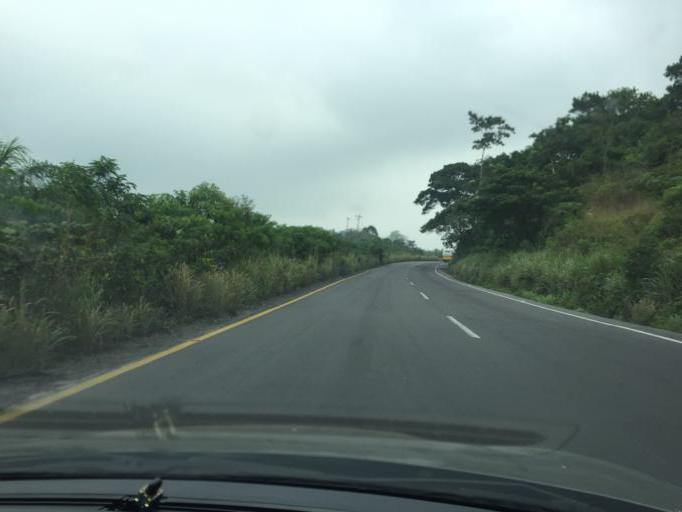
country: MX
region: Veracruz
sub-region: Moloacan
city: Tlacuilolapan
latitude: 18.0522
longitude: -94.2154
